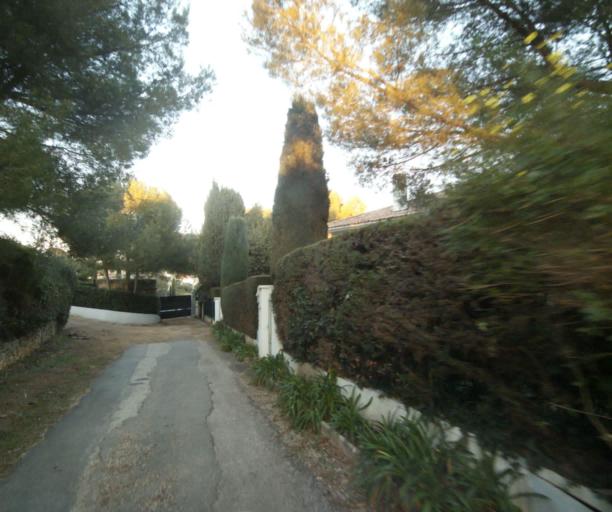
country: FR
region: Provence-Alpes-Cote d'Azur
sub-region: Departement des Alpes-Maritimes
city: Antibes
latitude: 43.5567
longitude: 7.1319
